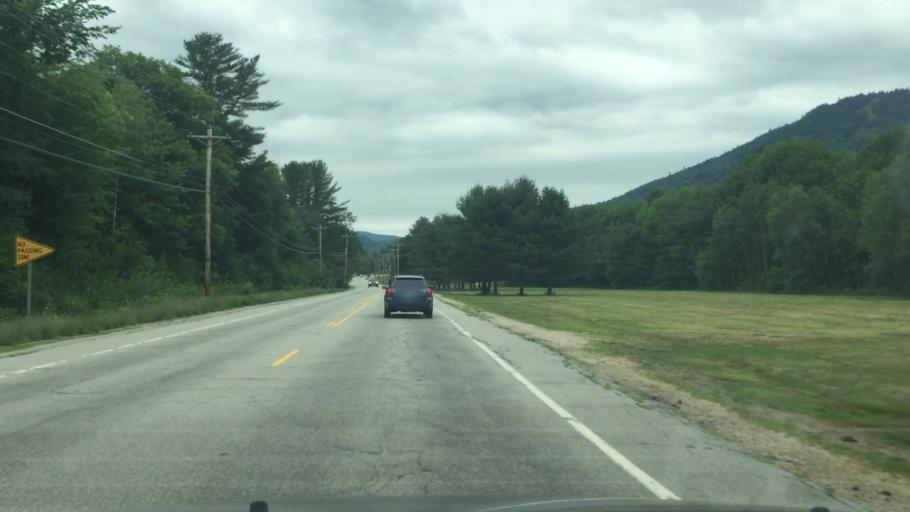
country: US
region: New Hampshire
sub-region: Carroll County
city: North Conway
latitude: 44.0807
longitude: -71.2514
